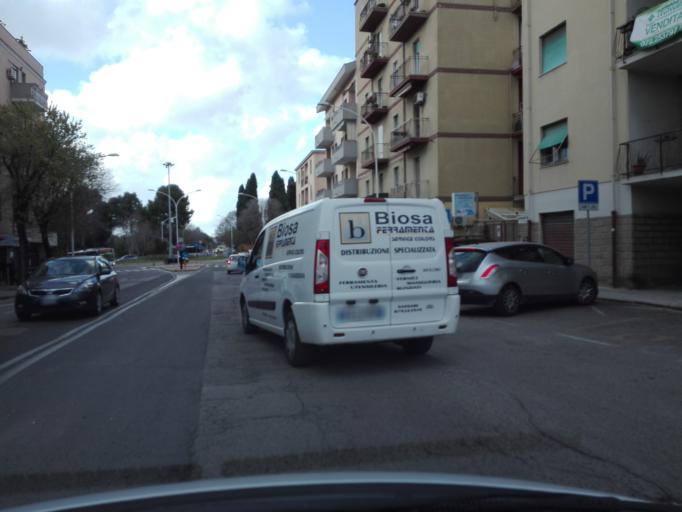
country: IT
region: Sardinia
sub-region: Provincia di Sassari
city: Sassari
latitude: 40.7364
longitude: 8.5608
